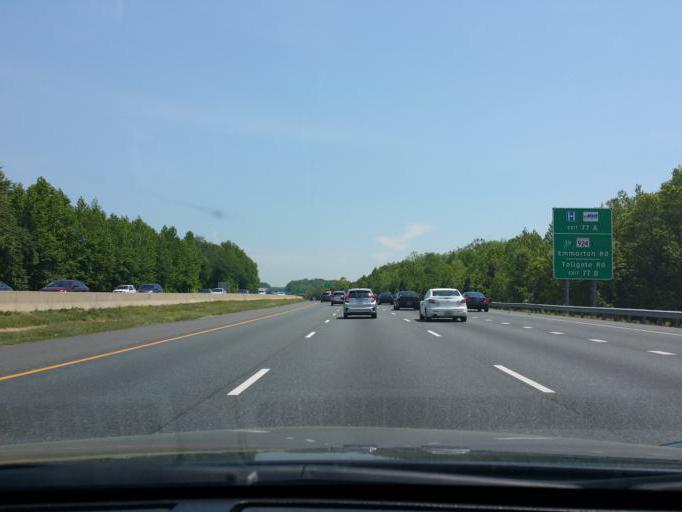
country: US
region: Maryland
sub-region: Harford County
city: Joppatowne
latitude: 39.4478
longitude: -76.3276
